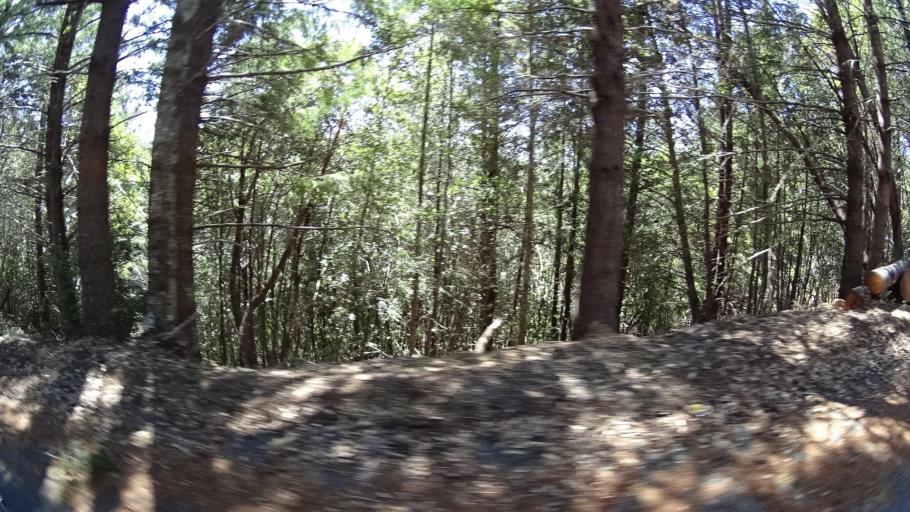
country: US
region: California
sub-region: Humboldt County
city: Redway
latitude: 40.1507
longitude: -124.0288
